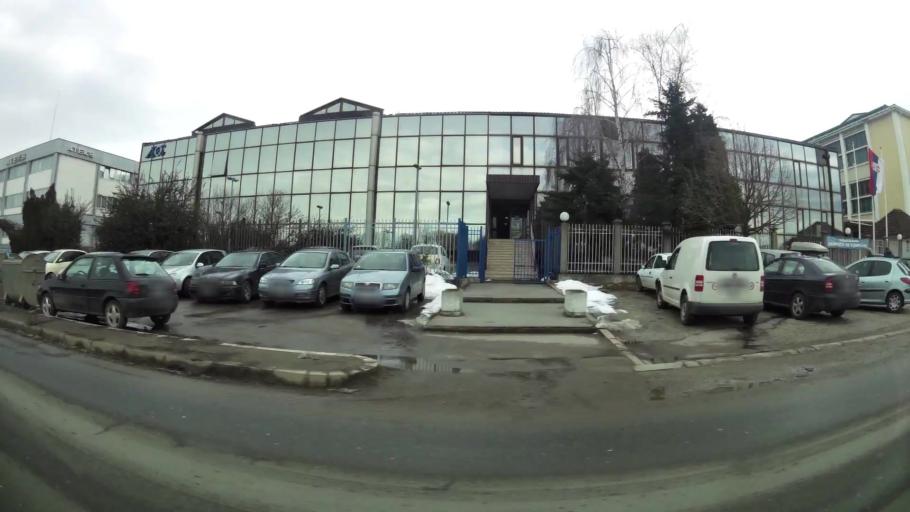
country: RS
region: Central Serbia
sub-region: Belgrade
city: Cukarica
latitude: 44.7620
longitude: 20.4046
